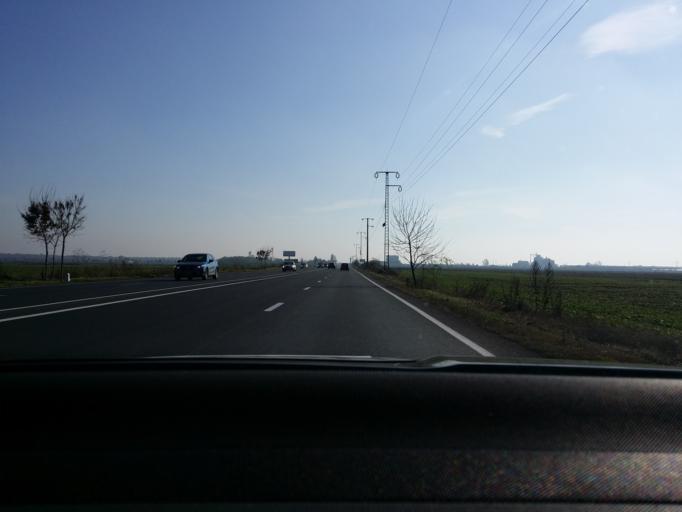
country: RO
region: Prahova
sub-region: Oras Baicoi
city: Tintea
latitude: 44.9933
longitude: 25.9054
